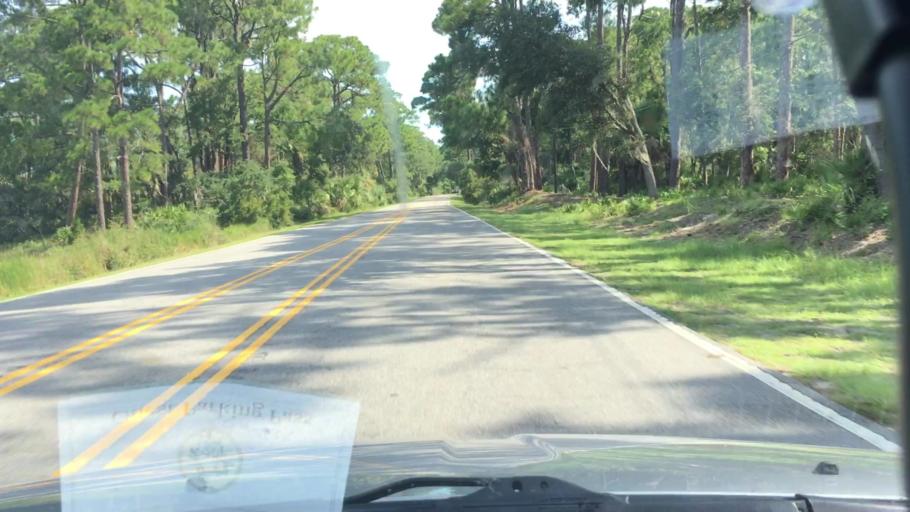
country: US
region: South Carolina
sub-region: Beaufort County
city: Beaufort
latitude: 32.3754
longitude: -80.4461
